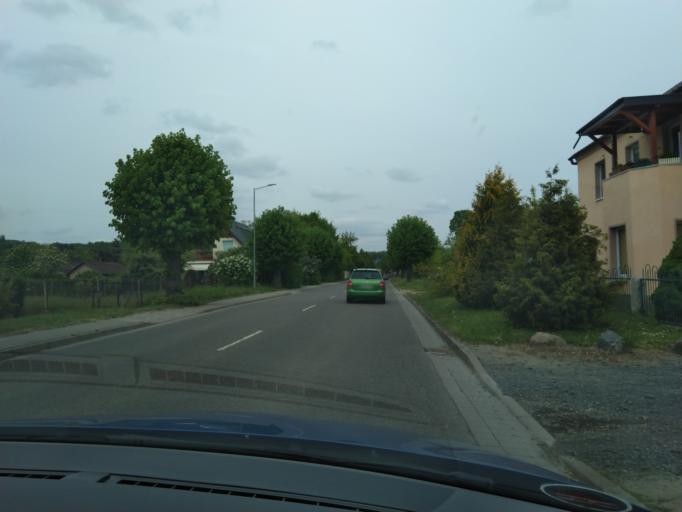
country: DE
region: Brandenburg
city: Oderberg
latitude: 52.8585
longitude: 14.0390
